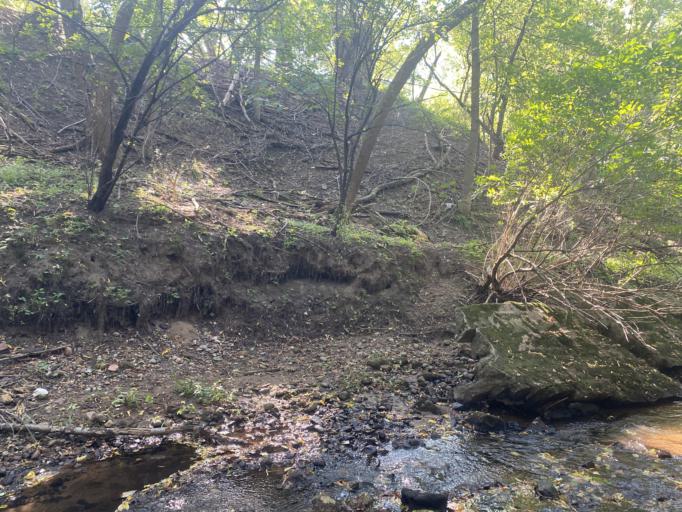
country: US
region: Wisconsin
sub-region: Dunn County
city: Menomonie
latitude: 44.8658
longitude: -91.9277
